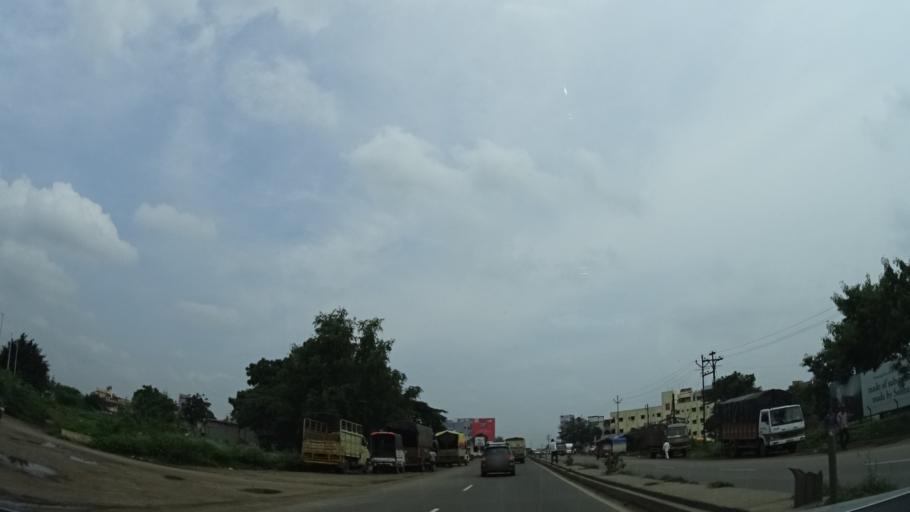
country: IN
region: Maharashtra
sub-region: Pune Division
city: Koregaon
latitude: 18.6698
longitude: 74.0998
